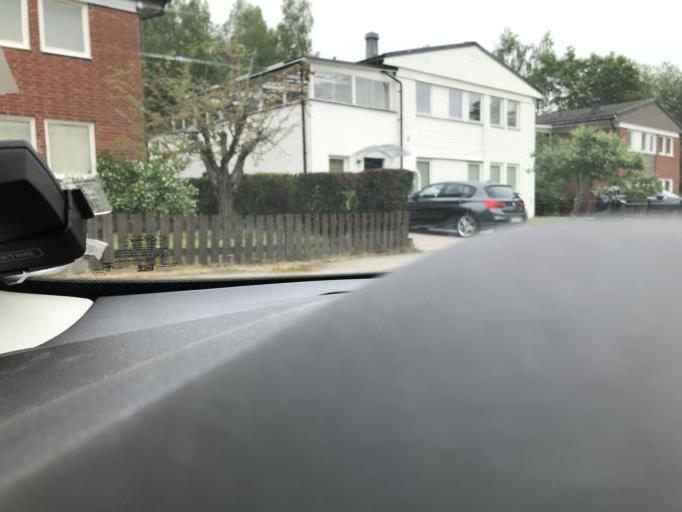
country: SE
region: Stockholm
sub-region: Botkyrka Kommun
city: Tumba
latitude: 59.2087
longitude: 17.8288
